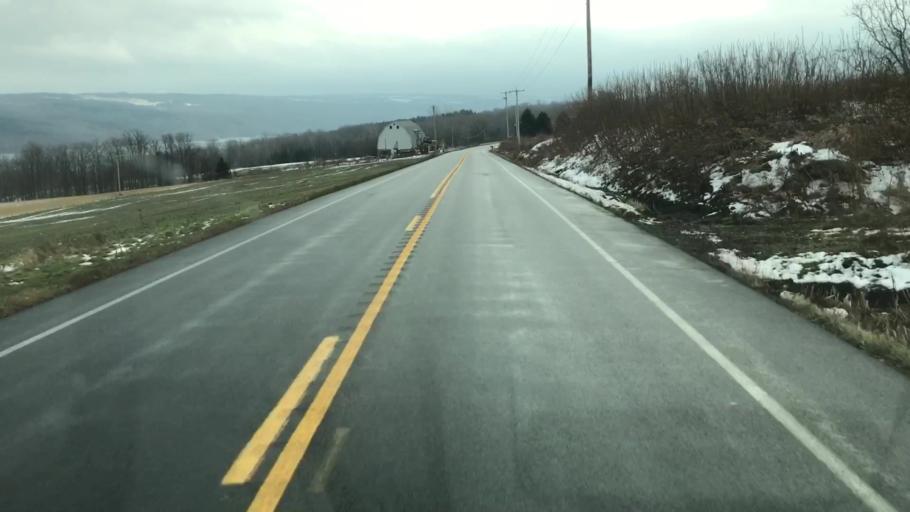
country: US
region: New York
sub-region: Onondaga County
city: Skaneateles
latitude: 42.8343
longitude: -76.3582
